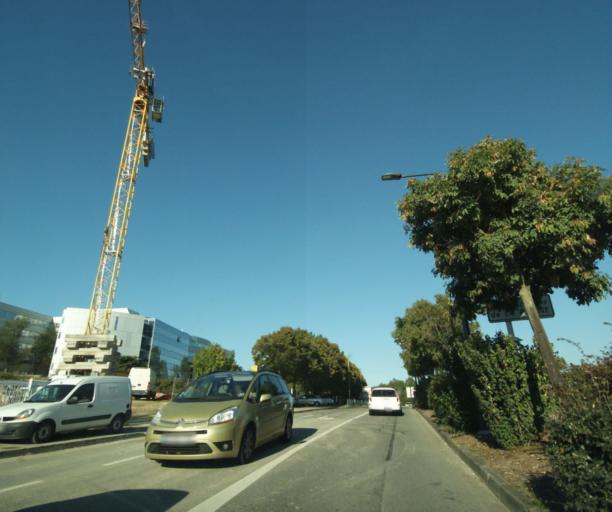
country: FR
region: Midi-Pyrenees
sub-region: Departement de la Haute-Garonne
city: Ramonville-Saint-Agne
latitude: 43.5734
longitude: 1.4935
